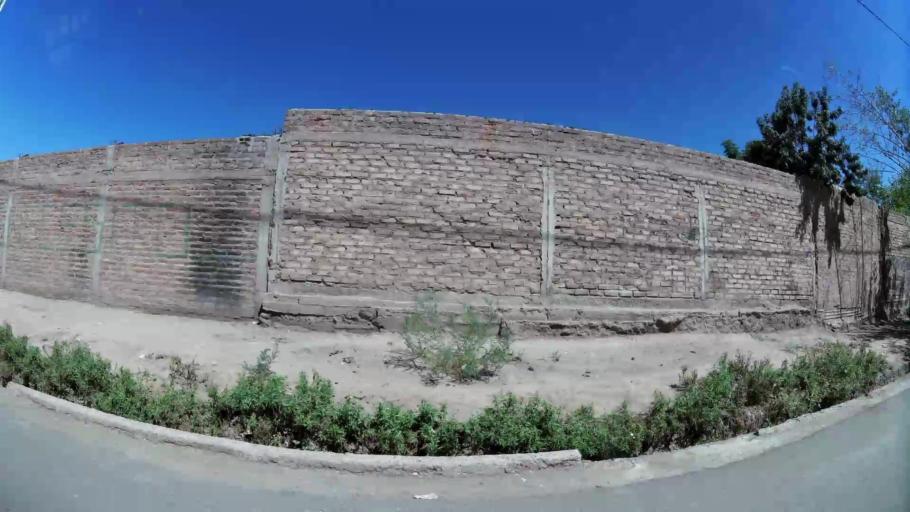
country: AR
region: Mendoza
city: Villa Nueva
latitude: -32.8801
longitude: -68.8001
